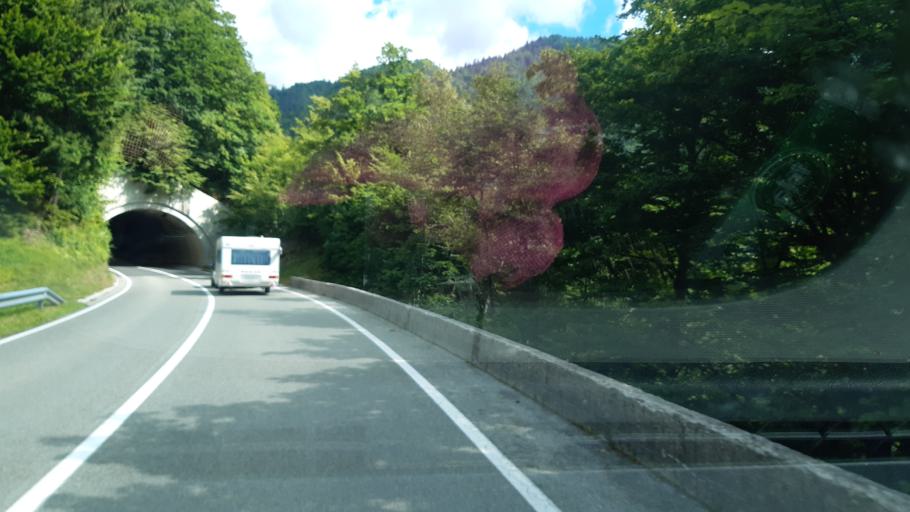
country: SI
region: Trzic
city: Trzic
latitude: 46.3675
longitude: 14.3067
